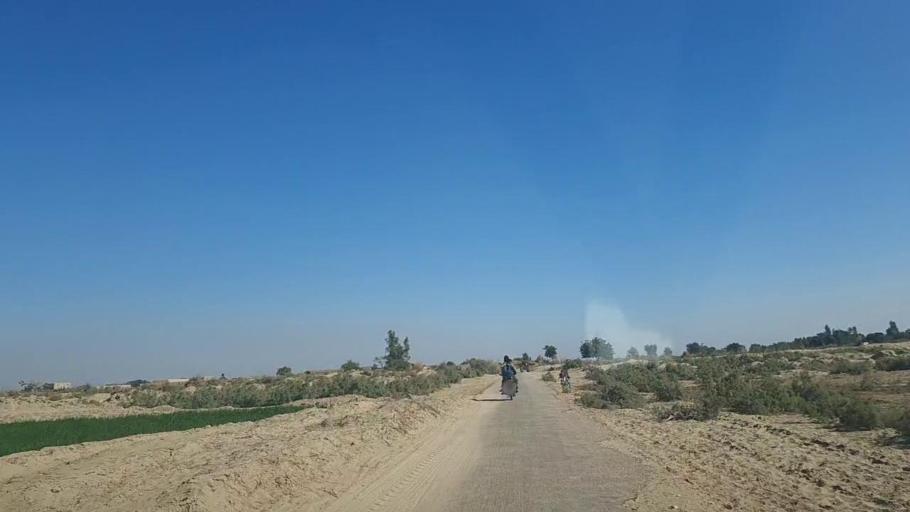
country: PK
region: Sindh
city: Khadro
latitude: 26.2094
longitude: 68.8398
